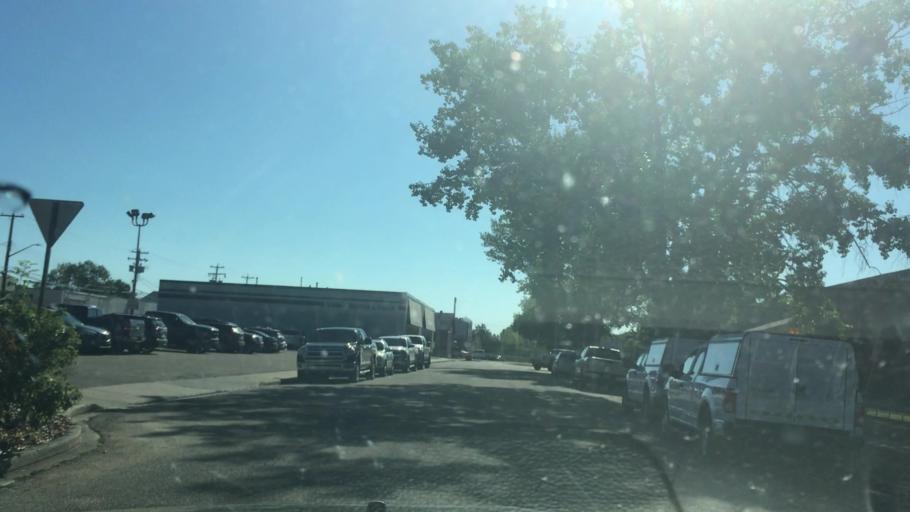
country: CA
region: Alberta
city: Leduc
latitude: 53.2640
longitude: -113.5503
